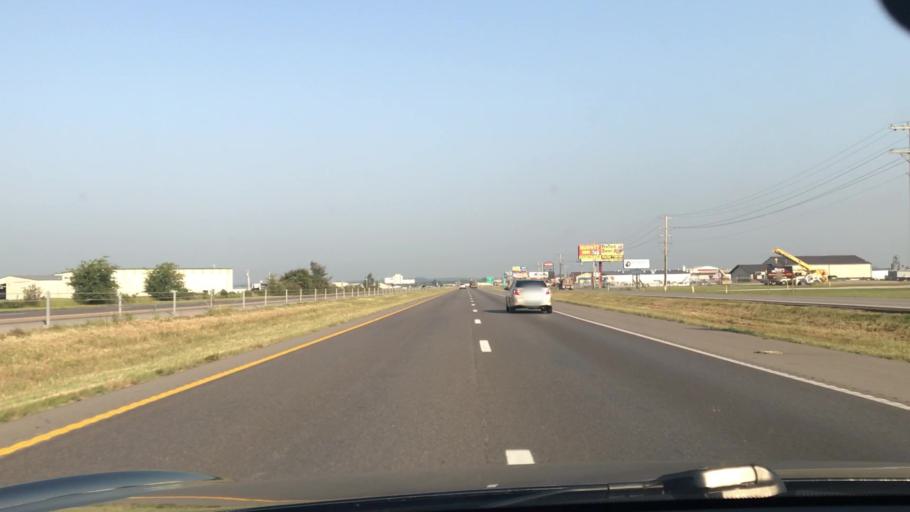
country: US
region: Missouri
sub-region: Scott County
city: Scott City
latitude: 37.2249
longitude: -89.5559
